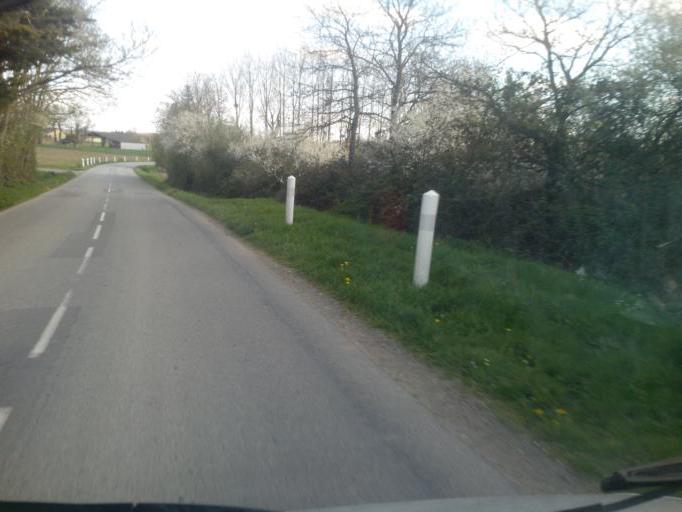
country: FR
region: Brittany
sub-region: Departement d'Ille-et-Vilaine
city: Maure-de-Bretagne
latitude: 47.9315
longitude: -2.0034
